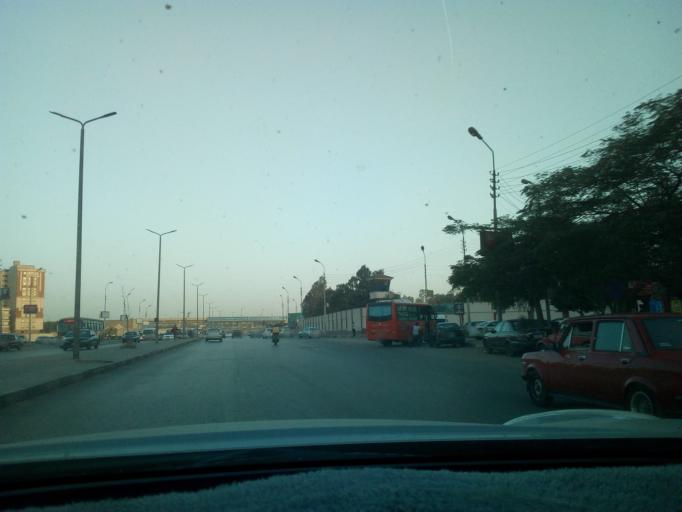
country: EG
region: Muhafazat al Qalyubiyah
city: Al Khankah
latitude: 30.1172
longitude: 31.3621
